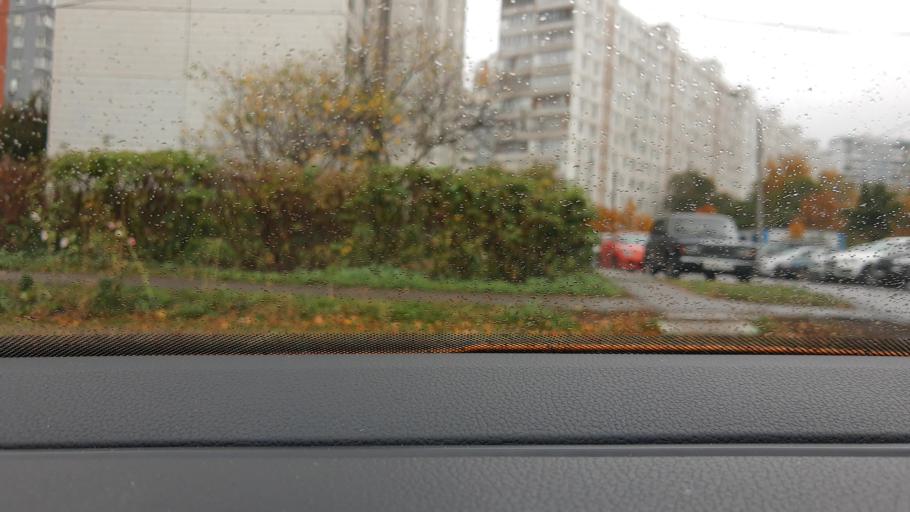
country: RU
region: Moscow
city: Strogino
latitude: 55.7974
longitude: 37.3943
